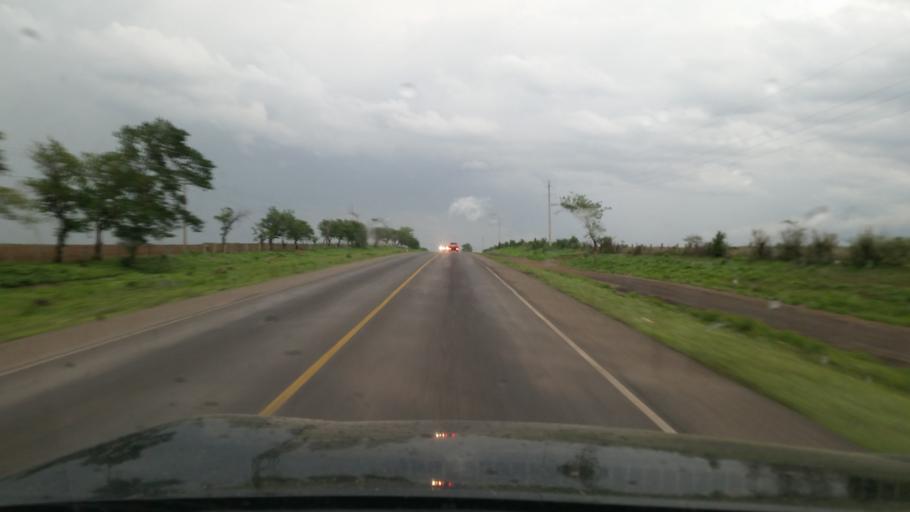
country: NI
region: Chinandega
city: Puerto Morazan
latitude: 12.7907
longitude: -87.0165
